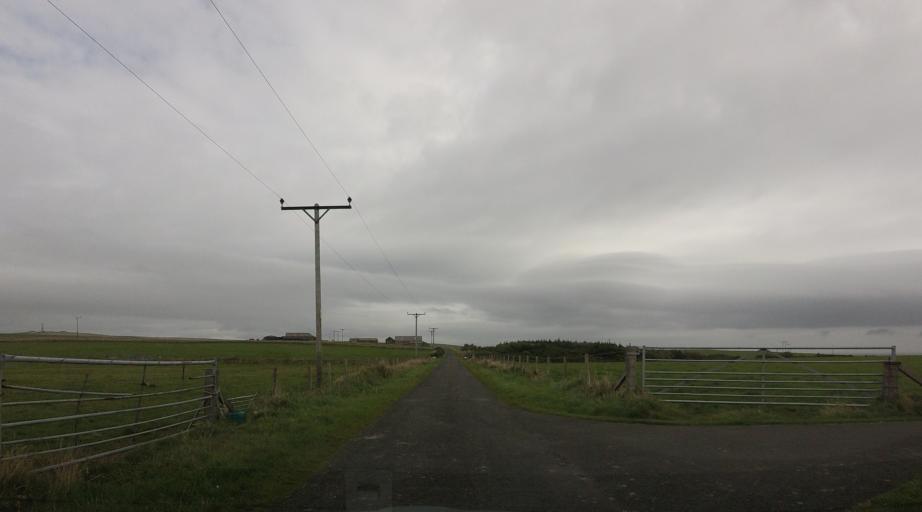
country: GB
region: Scotland
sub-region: Orkney Islands
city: Orkney
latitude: 58.7655
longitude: -2.9568
